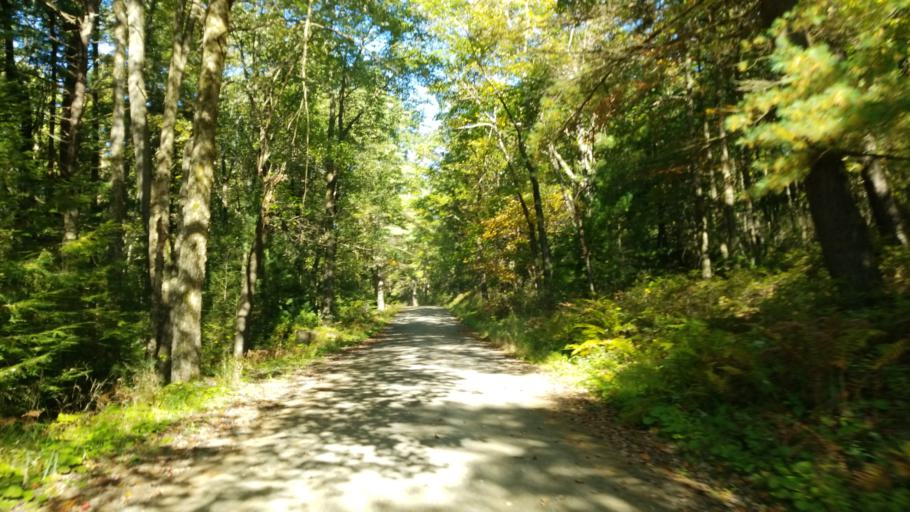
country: US
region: Pennsylvania
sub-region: Clearfield County
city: Hyde
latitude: 41.0846
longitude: -78.5273
